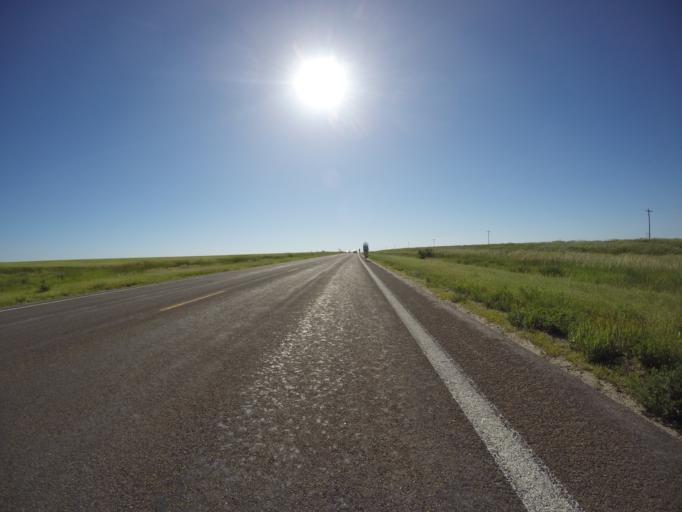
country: US
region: Kansas
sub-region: Norton County
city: Norton
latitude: 39.8280
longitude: -100.0144
